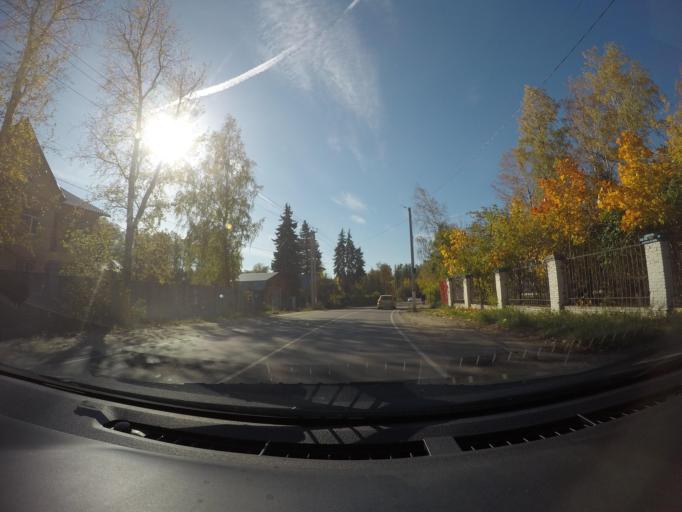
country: RU
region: Moskovskaya
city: Rodniki
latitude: 55.6459
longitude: 38.0536
